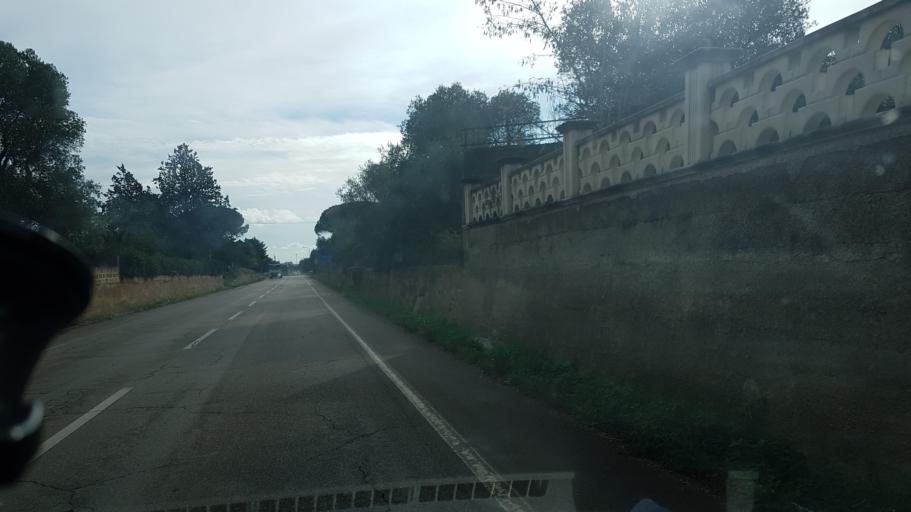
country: IT
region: Apulia
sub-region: Provincia di Brindisi
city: San Vito dei Normanni
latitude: 40.6719
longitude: 17.6928
